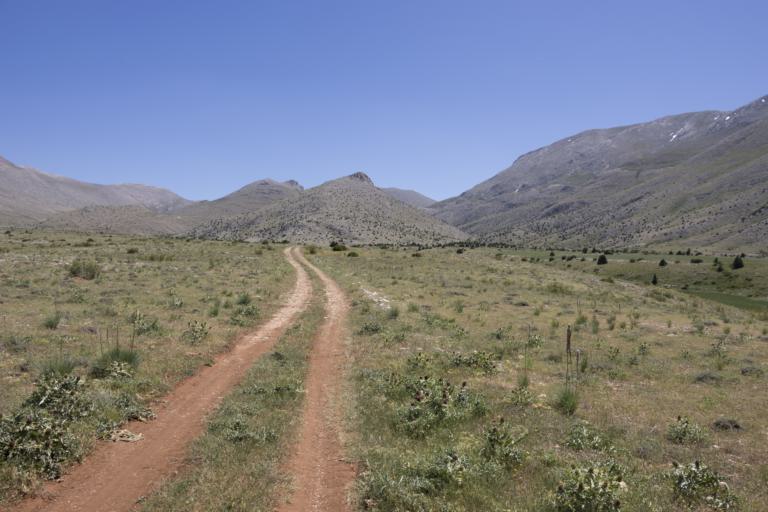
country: TR
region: Kayseri
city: Toklar
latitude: 38.3999
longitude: 36.1172
